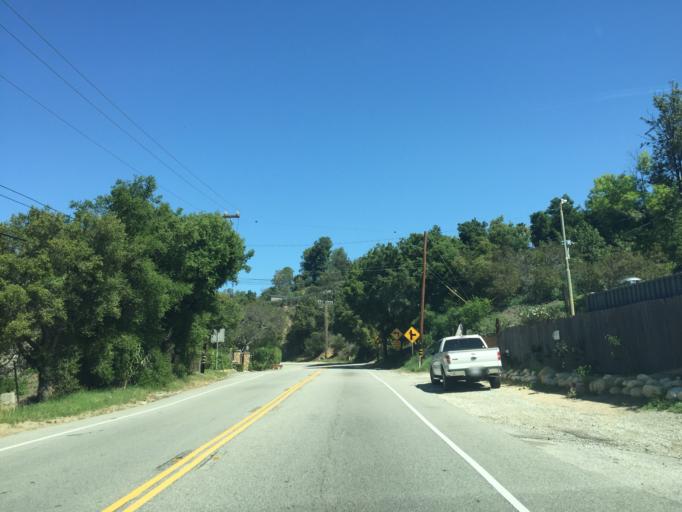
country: US
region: California
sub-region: Los Angeles County
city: Topanga
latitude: 34.1217
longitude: -118.5909
